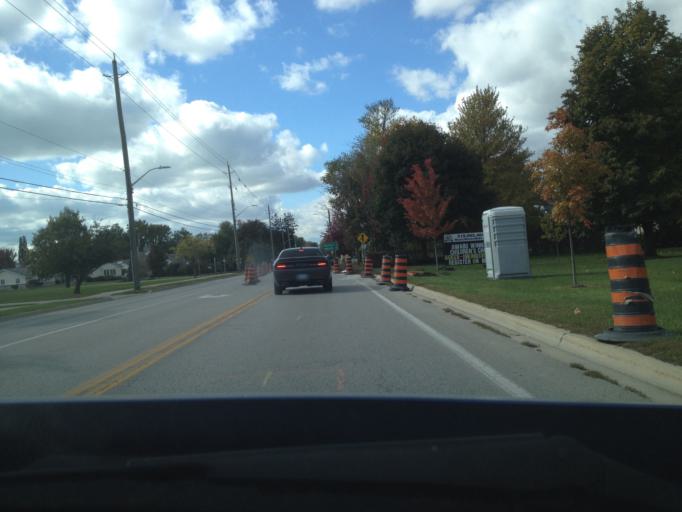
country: CA
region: Ontario
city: Amherstburg
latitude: 42.0342
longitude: -82.6061
